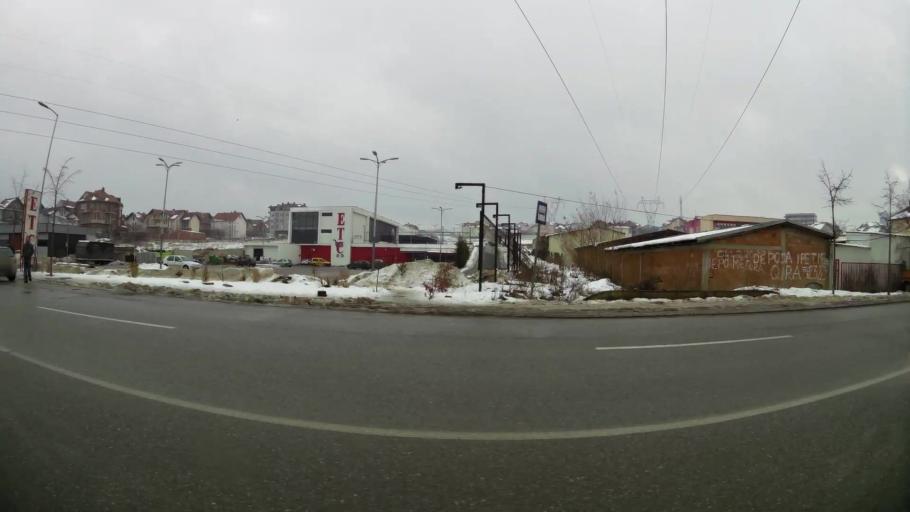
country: XK
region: Pristina
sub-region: Komuna e Prishtines
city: Pristina
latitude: 42.6943
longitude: 21.1604
